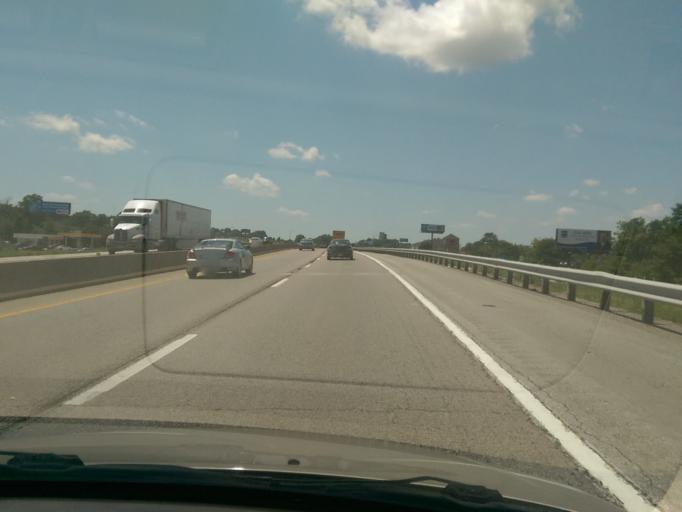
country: US
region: Missouri
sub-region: Boone County
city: Columbia
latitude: 38.9677
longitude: -92.3495
